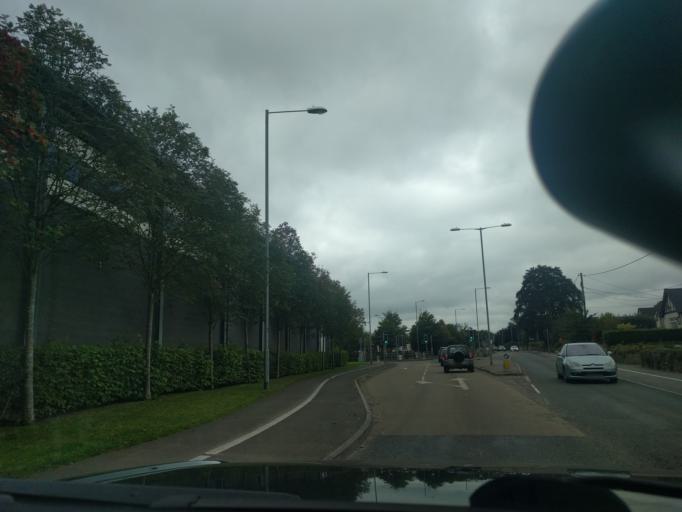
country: GB
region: England
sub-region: Wiltshire
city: Chippenham
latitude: 51.4512
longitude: -2.1344
